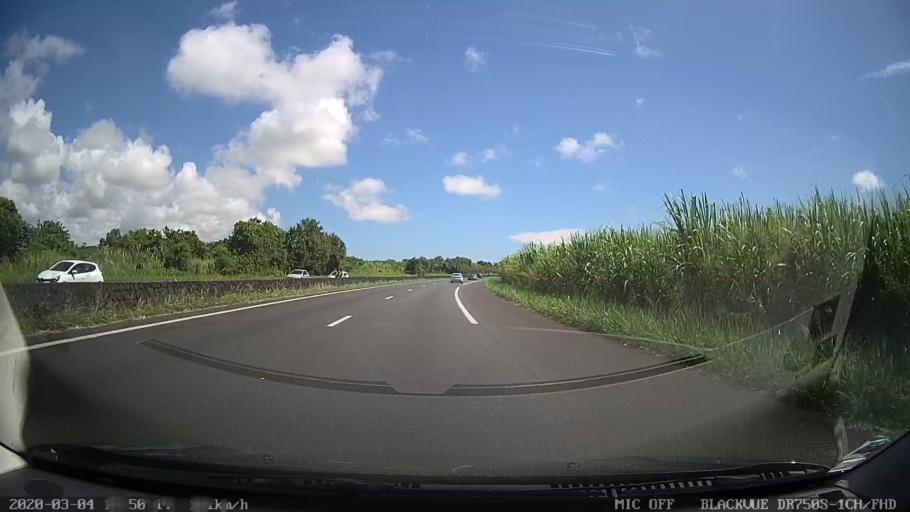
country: RE
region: Reunion
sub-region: Reunion
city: Saint-Andre
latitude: -20.9817
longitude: 55.6547
